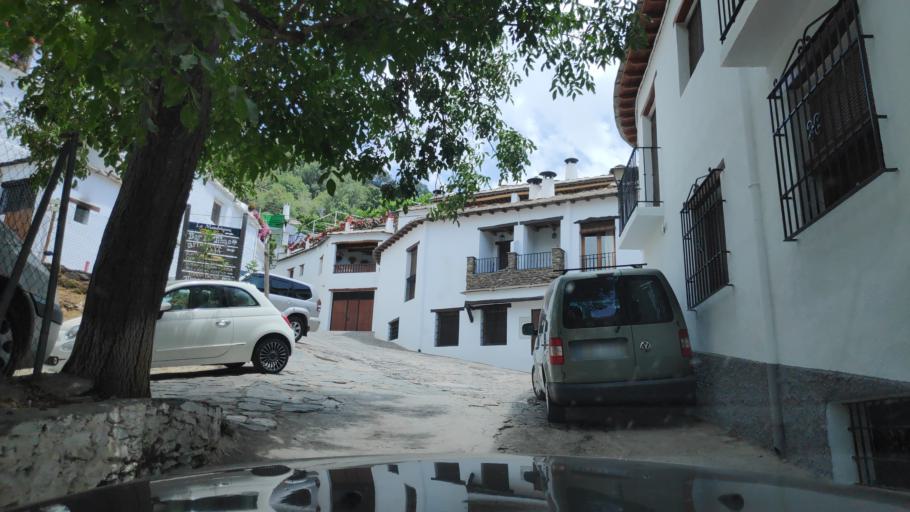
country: ES
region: Andalusia
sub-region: Provincia de Granada
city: Capileira
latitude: 36.9623
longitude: -3.3594
